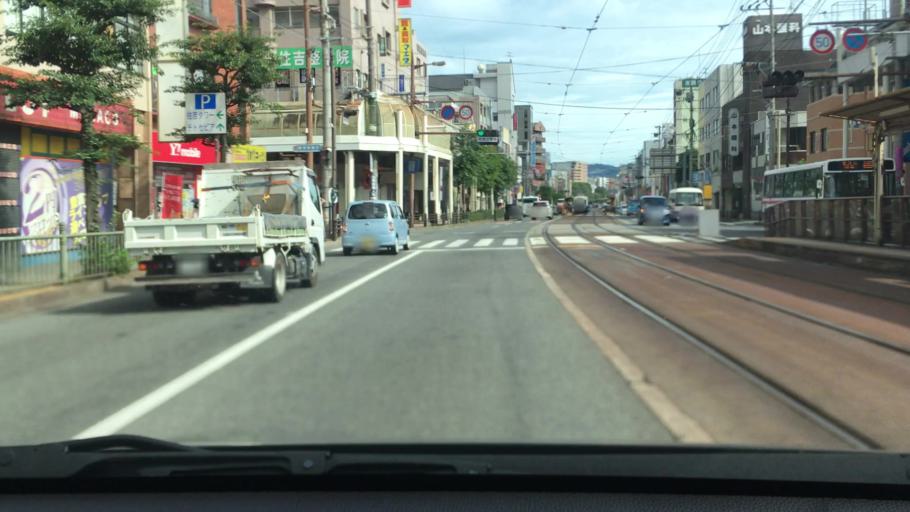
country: JP
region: Nagasaki
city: Obita
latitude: 32.7909
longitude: 129.8605
